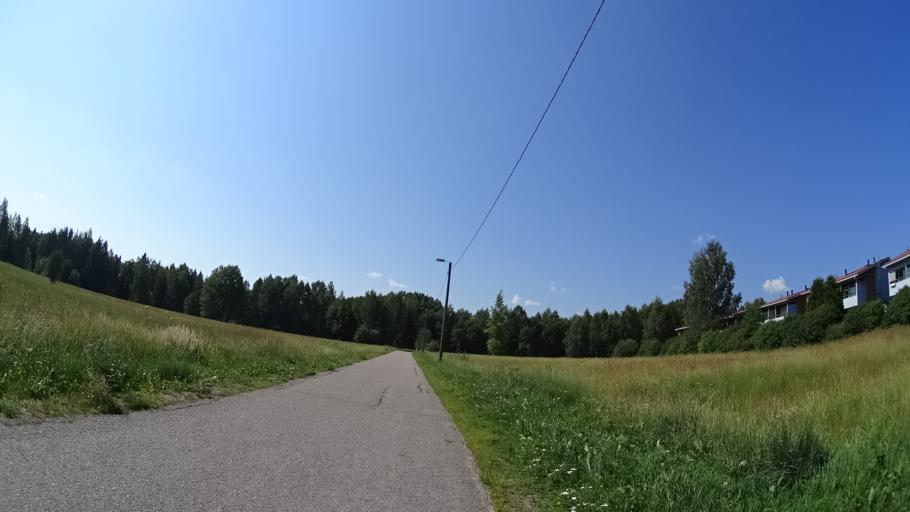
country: FI
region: Uusimaa
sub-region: Helsinki
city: Kerava
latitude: 60.3648
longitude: 25.0751
